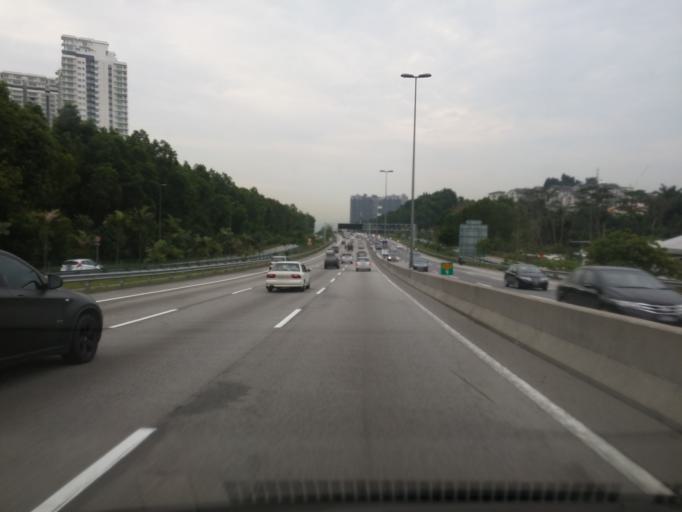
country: MY
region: Kuala Lumpur
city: Kuala Lumpur
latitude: 3.0756
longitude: 101.6896
